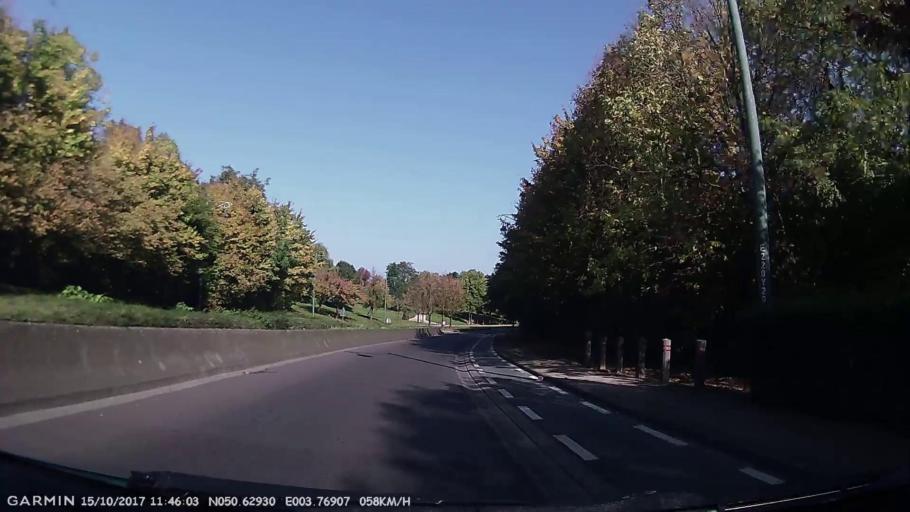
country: BE
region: Wallonia
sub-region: Province du Hainaut
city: Ath
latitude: 50.6294
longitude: 3.7690
